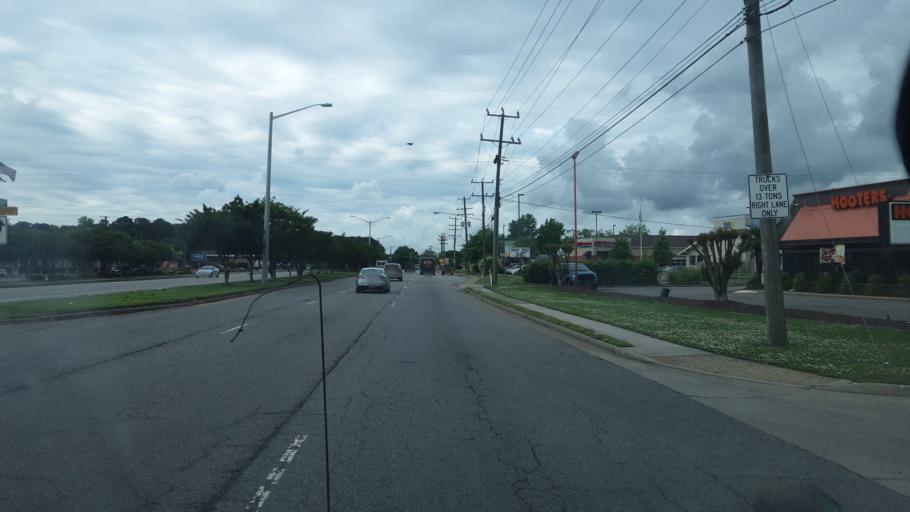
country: US
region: Virginia
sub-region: City of Virginia Beach
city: Virginia Beach
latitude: 36.7891
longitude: -75.9978
